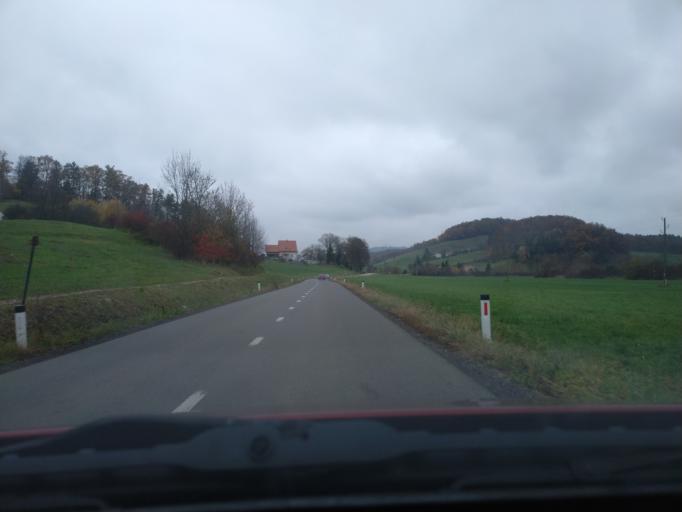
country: SI
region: Kungota
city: Zgornja Kungota
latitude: 46.6436
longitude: 15.6135
